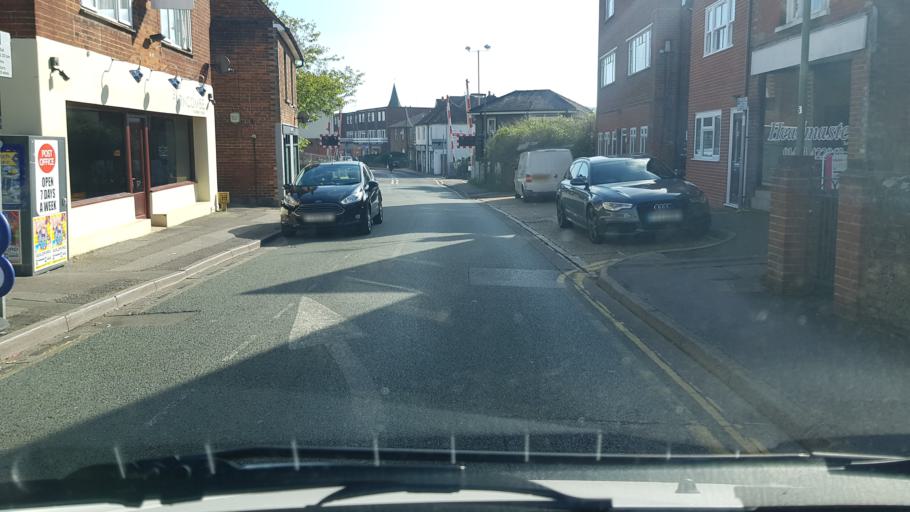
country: GB
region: England
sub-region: Surrey
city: Godalming
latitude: 51.1962
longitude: -0.6067
